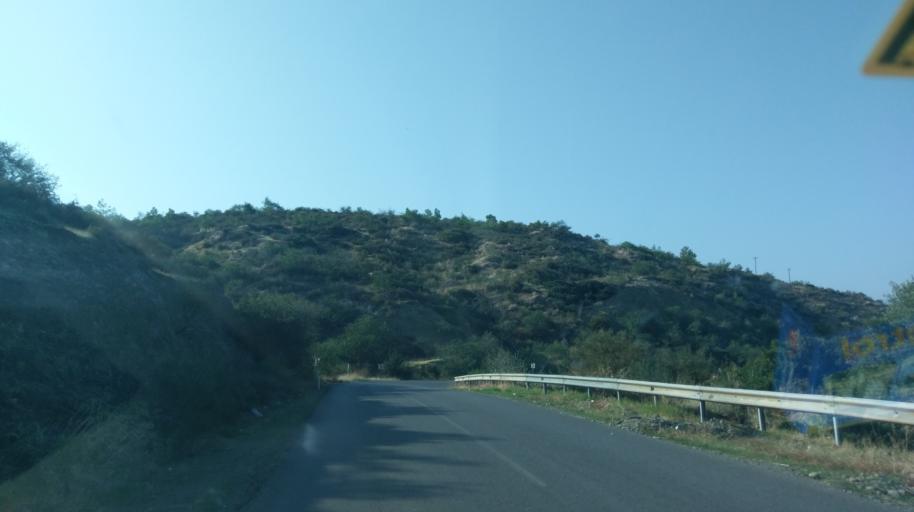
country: CY
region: Lefkosia
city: Lefka
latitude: 35.1517
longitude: 32.7938
